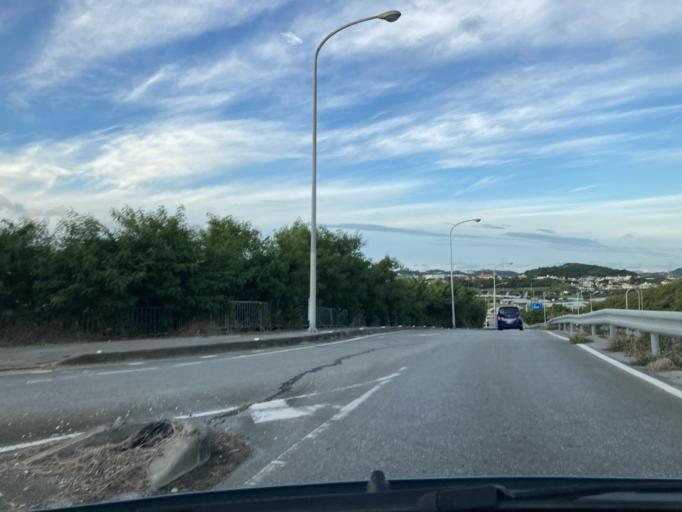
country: JP
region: Okinawa
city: Tomigusuku
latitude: 26.1737
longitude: 127.7270
